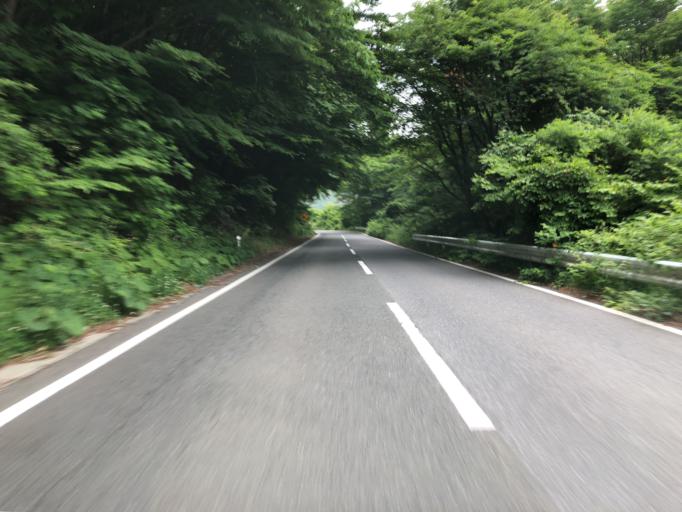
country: JP
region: Fukushima
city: Funehikimachi-funehiki
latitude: 37.3831
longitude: 140.7111
